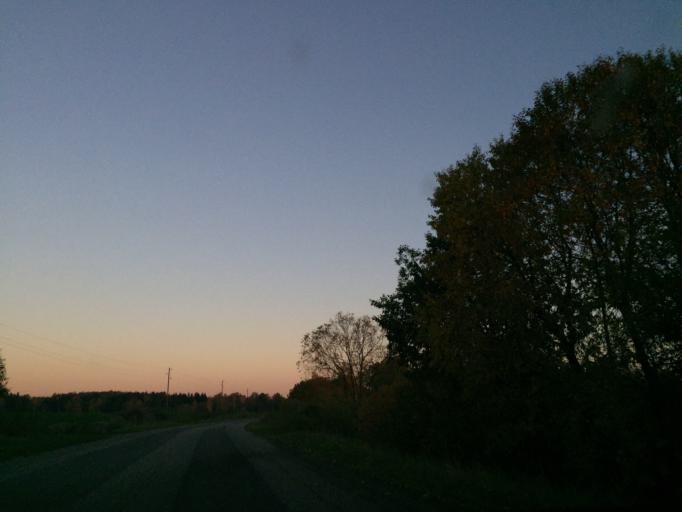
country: LT
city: Vieksniai
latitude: 56.3992
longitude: 22.5468
